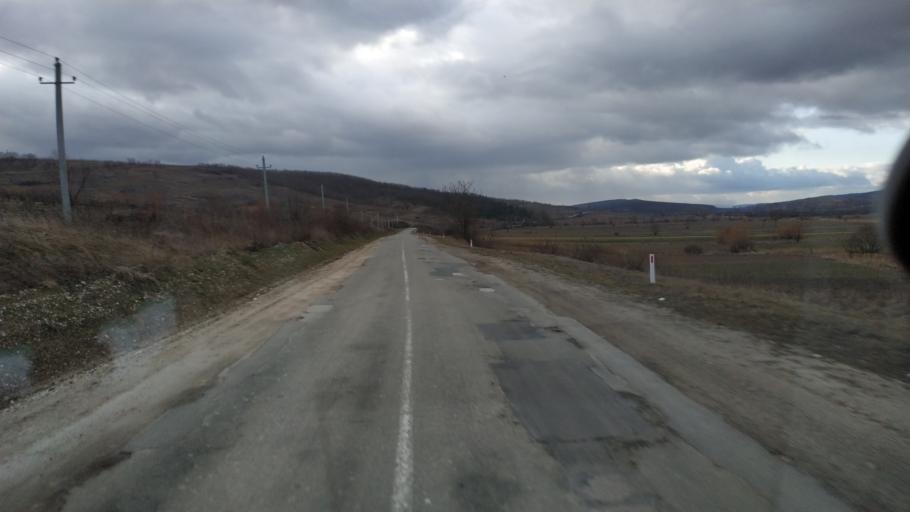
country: MD
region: Calarasi
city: Calarasi
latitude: 47.3124
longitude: 28.3510
